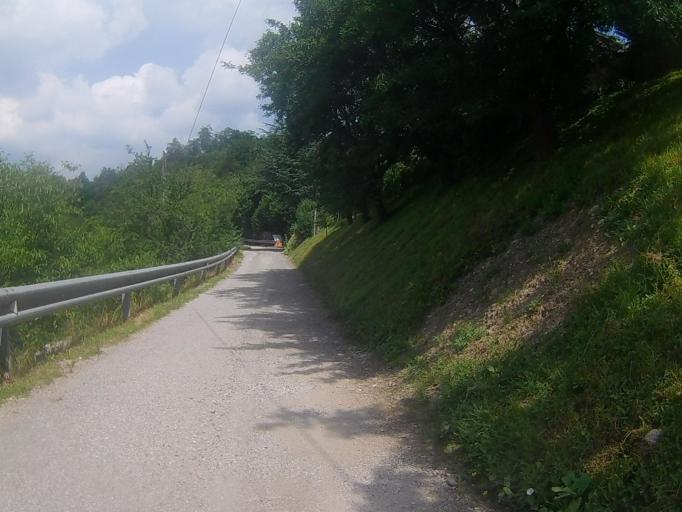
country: SI
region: Maribor
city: Bresternica
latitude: 46.5887
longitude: 15.5896
